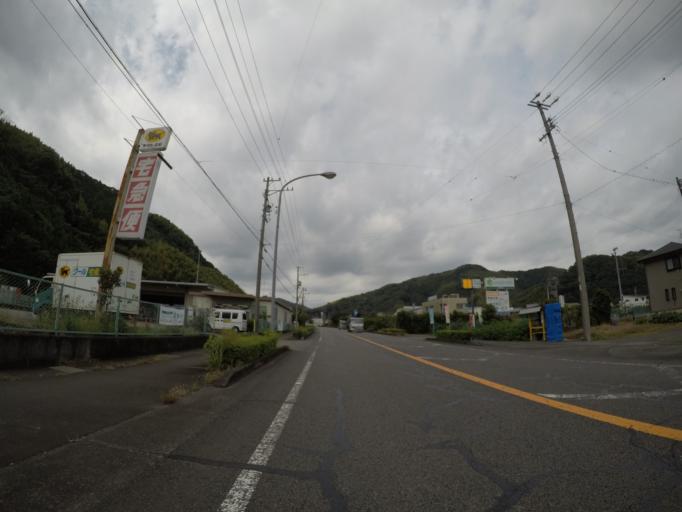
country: JP
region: Shizuoka
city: Fujieda
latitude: 34.8759
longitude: 138.2242
